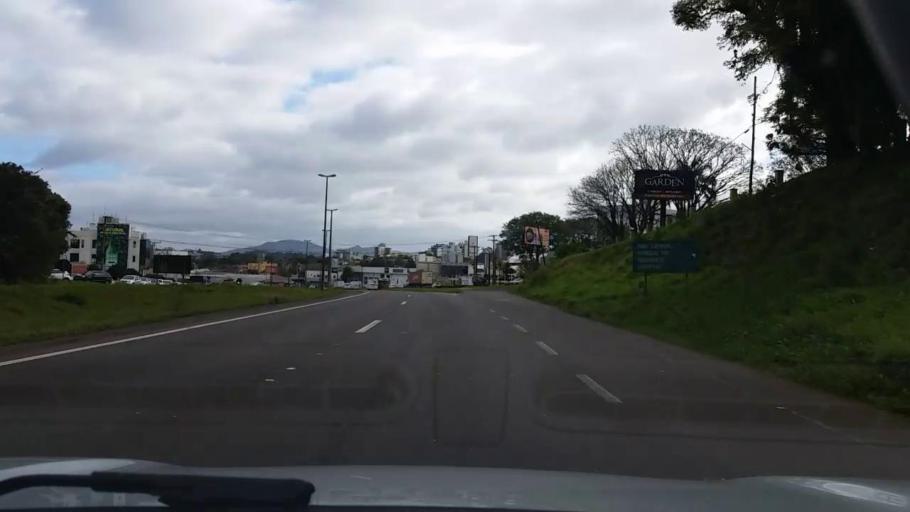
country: BR
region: Rio Grande do Sul
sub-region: Lajeado
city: Lajeado
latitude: -29.4579
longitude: -51.9568
